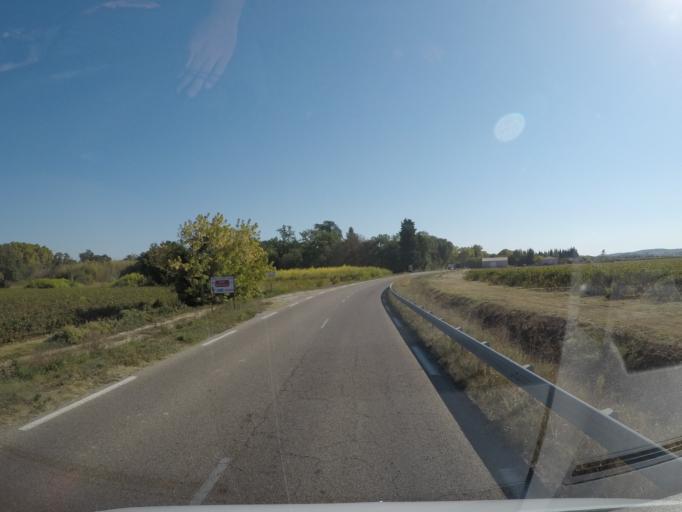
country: FR
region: Languedoc-Roussillon
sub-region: Departement du Gard
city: Ribaute-les-Tavernes
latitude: 44.0246
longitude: 4.0696
